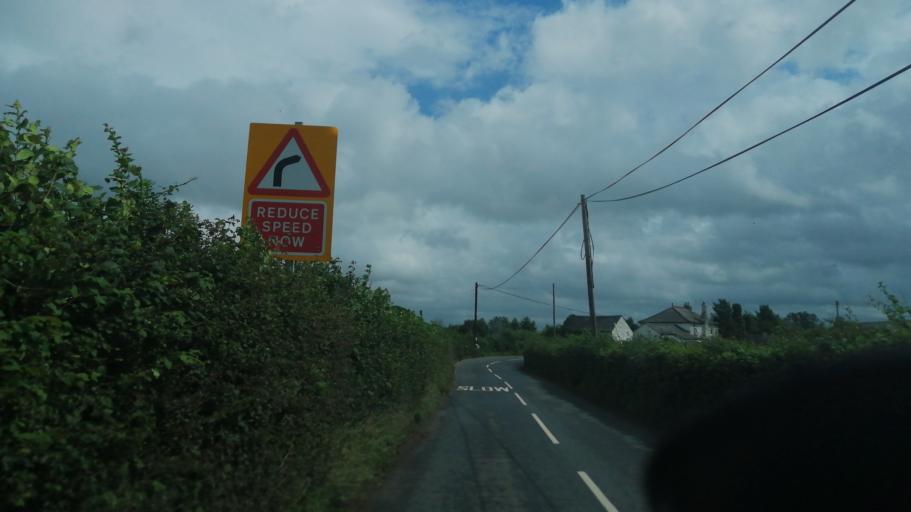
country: GB
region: England
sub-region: Herefordshire
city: Thruxton
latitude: 52.0083
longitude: -2.8050
